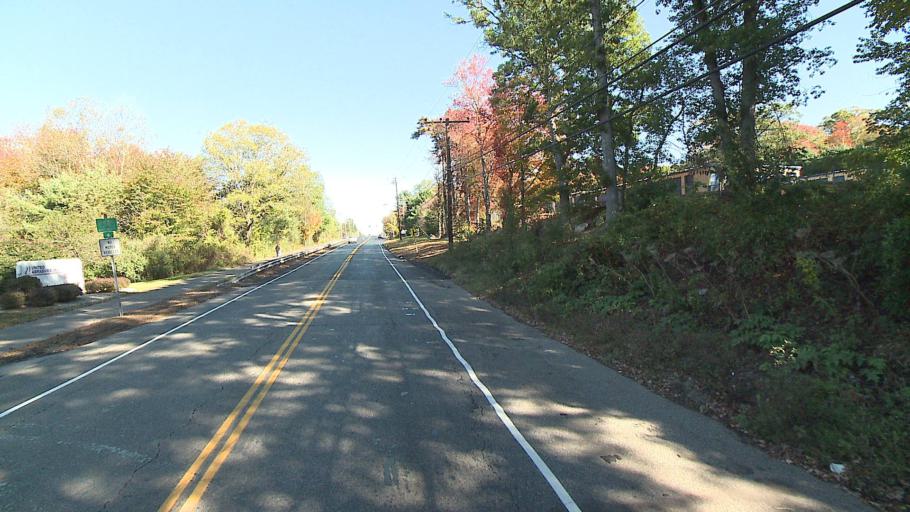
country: US
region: Connecticut
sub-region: Windham County
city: Willimantic
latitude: 41.7304
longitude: -72.1860
